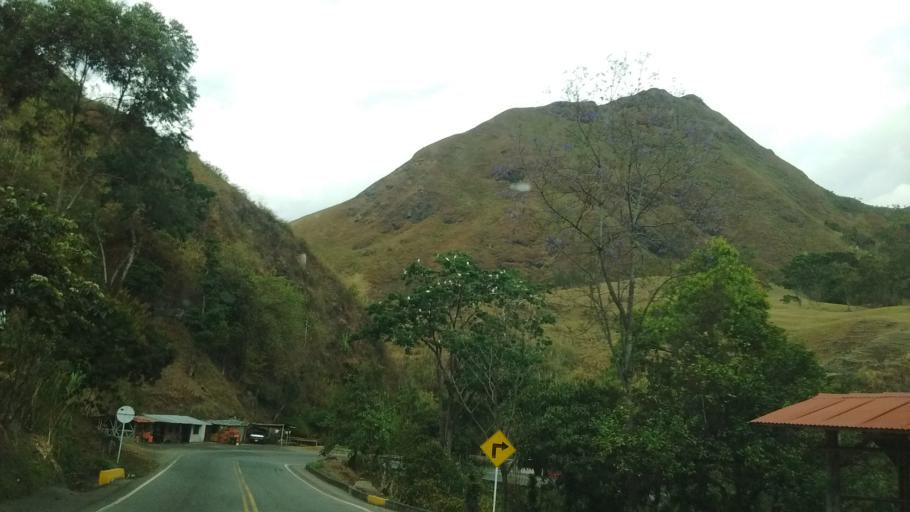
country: CO
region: Cauca
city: Rosas
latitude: 2.2836
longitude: -76.7013
